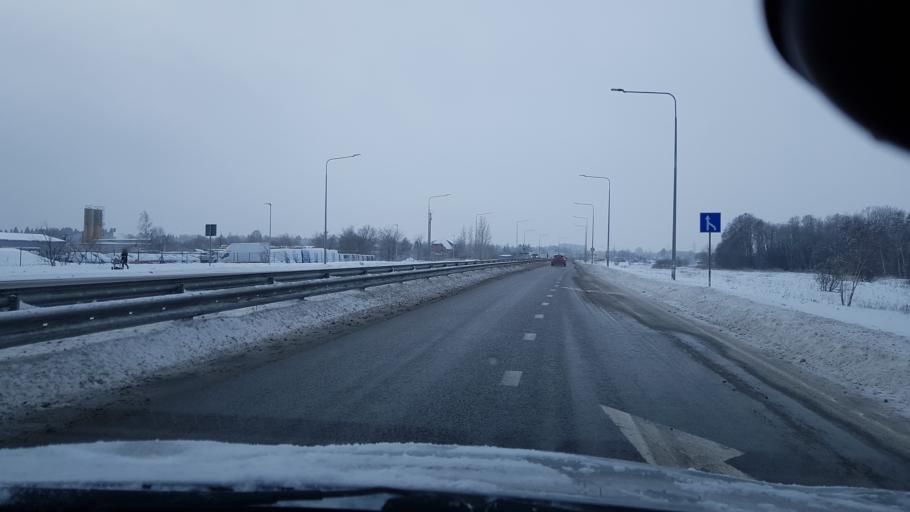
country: EE
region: Harju
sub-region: Saue vald
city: Laagri
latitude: 59.3946
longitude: 24.5916
